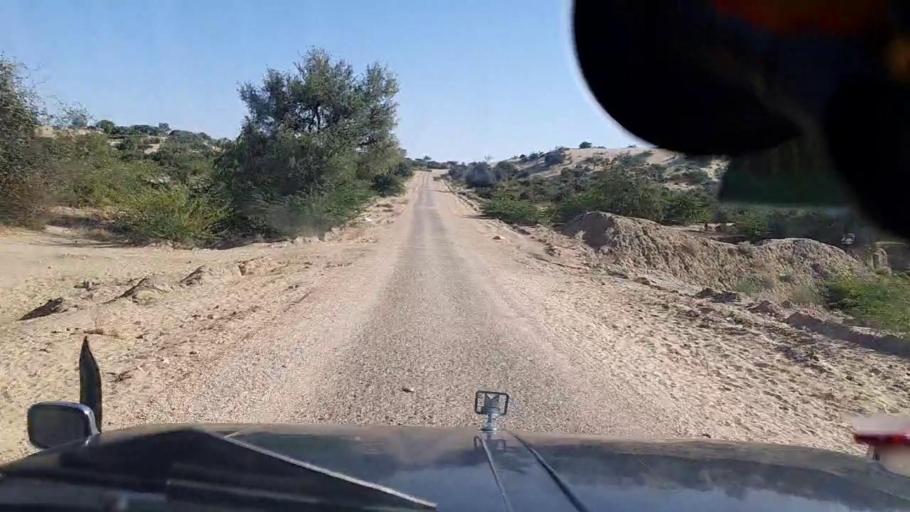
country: PK
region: Sindh
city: Diplo
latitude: 24.4743
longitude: 69.7928
